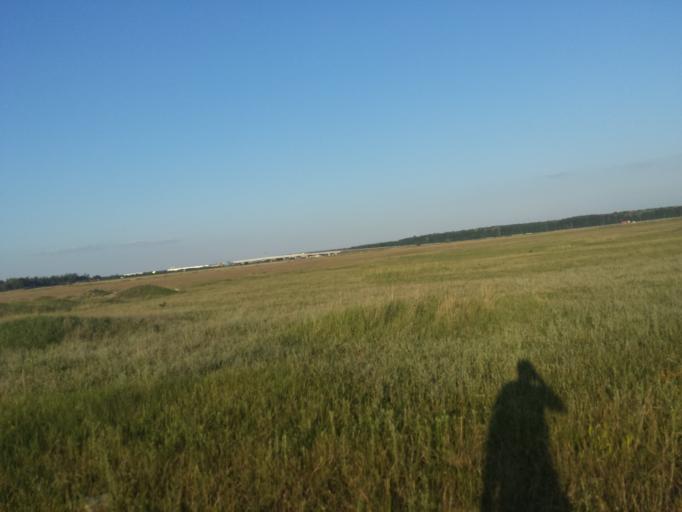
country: RO
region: Ilfov
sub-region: Comuna Tunari
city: Tunari
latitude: 44.5219
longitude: 26.1525
